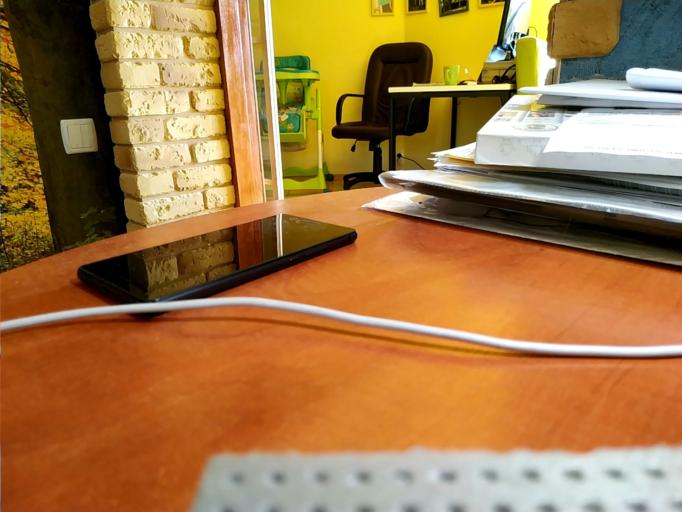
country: RU
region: Tverskaya
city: Kalashnikovo
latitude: 57.3709
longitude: 35.4115
